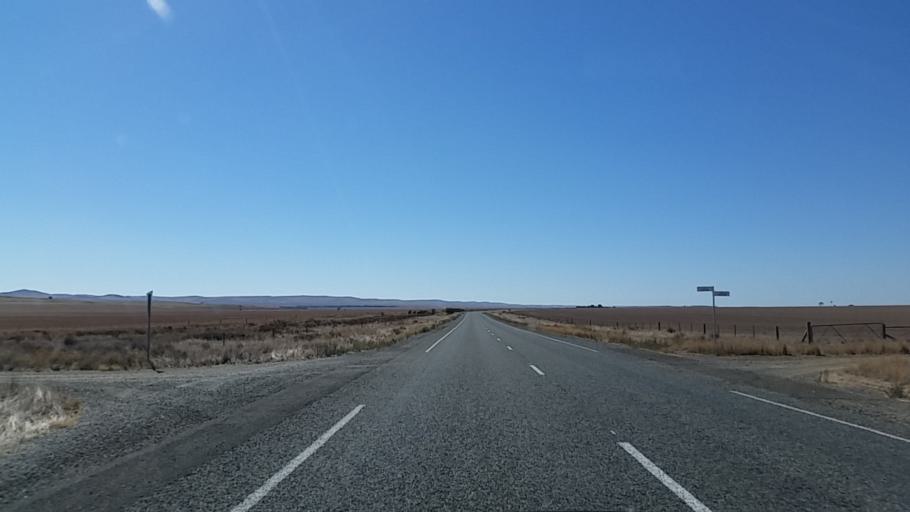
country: AU
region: South Australia
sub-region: Northern Areas
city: Jamestown
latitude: -33.2746
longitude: 138.8684
